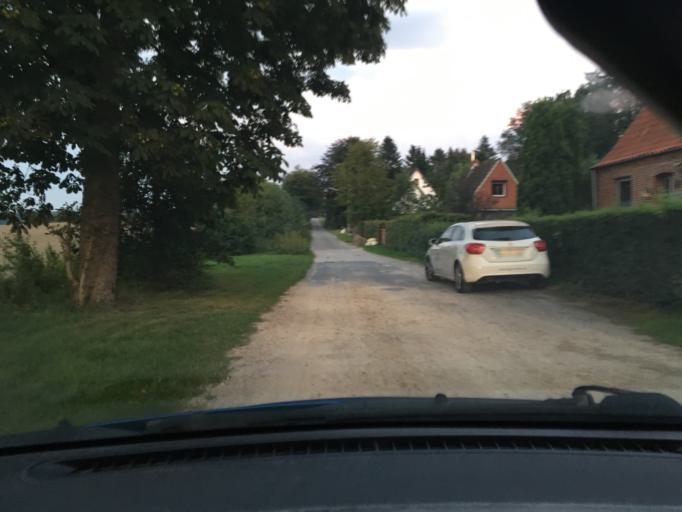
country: DE
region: Lower Saxony
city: Thomasburg
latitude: 53.1885
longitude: 10.6246
